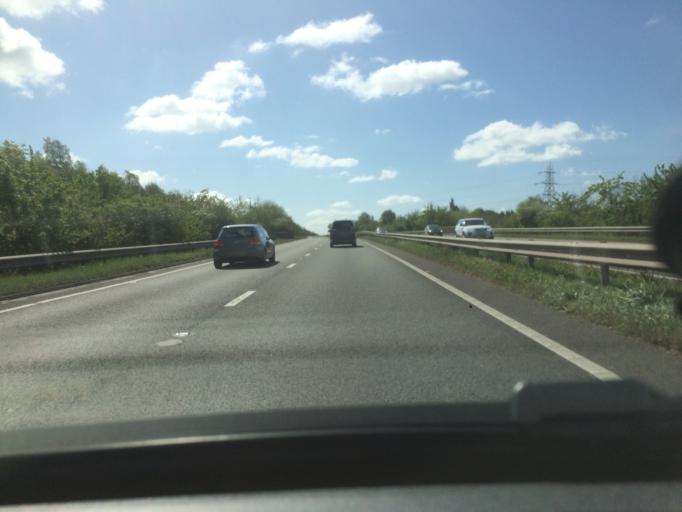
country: GB
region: Wales
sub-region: Wrexham
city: Rhosllanerchrugog
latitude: 53.0271
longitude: -3.0309
